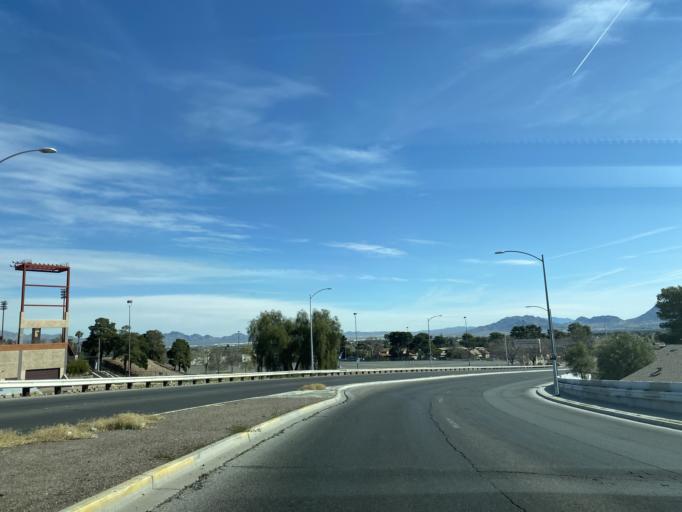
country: US
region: Nevada
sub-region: Clark County
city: Las Vegas
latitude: 36.1778
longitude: -115.1300
